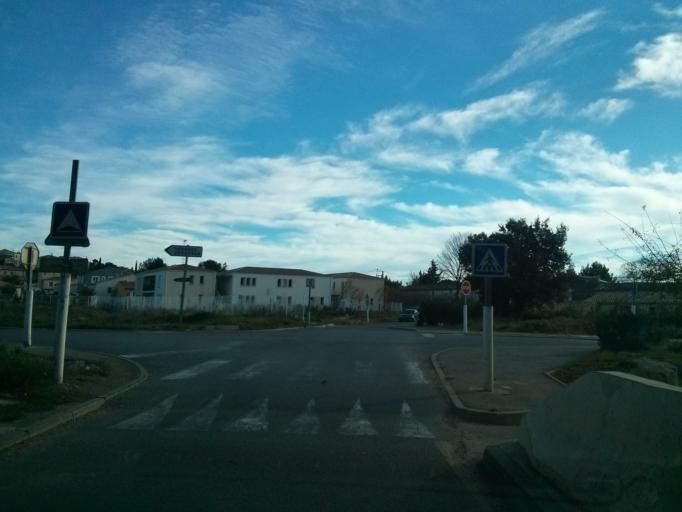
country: FR
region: Languedoc-Roussillon
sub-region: Departement du Gard
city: Mus
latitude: 43.7390
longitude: 4.1957
